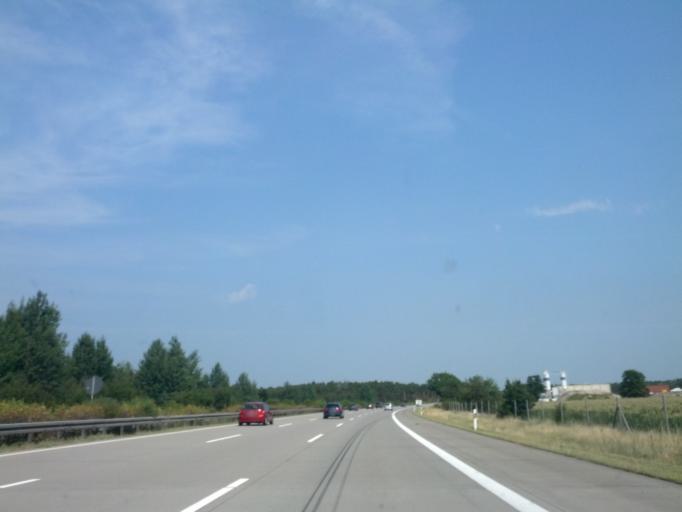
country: DE
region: Brandenburg
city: Borkheide
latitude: 52.1900
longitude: 12.8542
